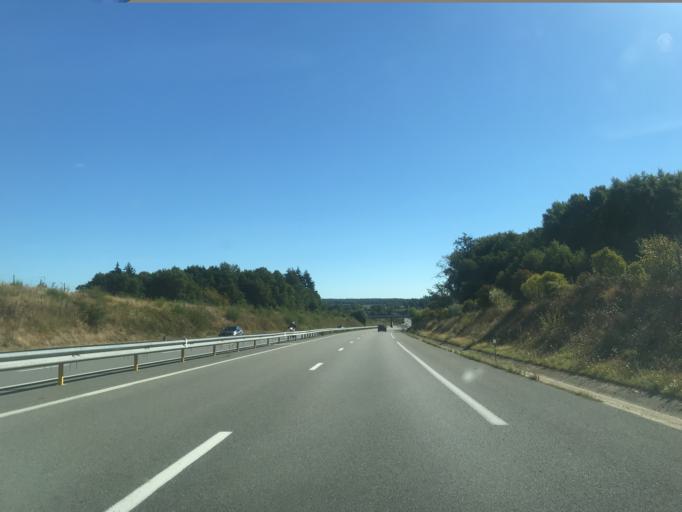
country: FR
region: Limousin
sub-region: Departement de la Creuse
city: Gouzon
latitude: 46.2371
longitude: 2.3225
